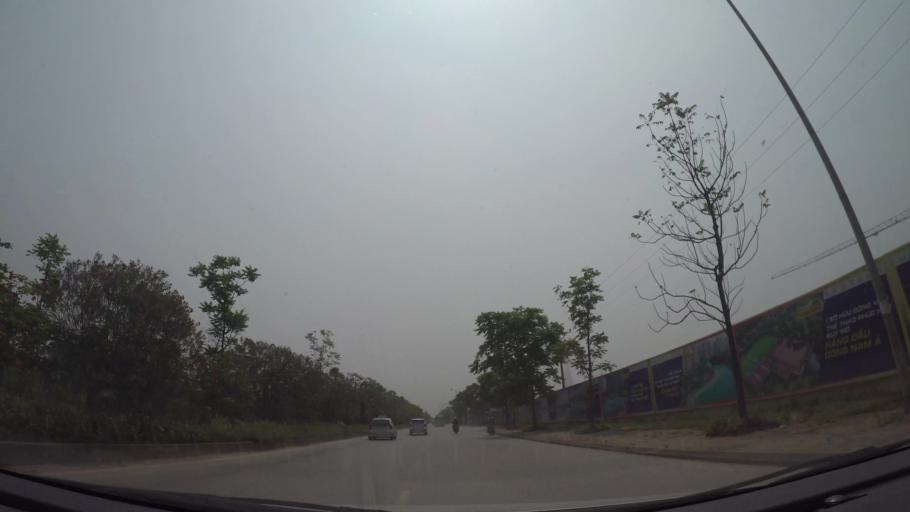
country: VN
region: Ha Noi
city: Cau Dien
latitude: 21.0077
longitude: 105.7543
